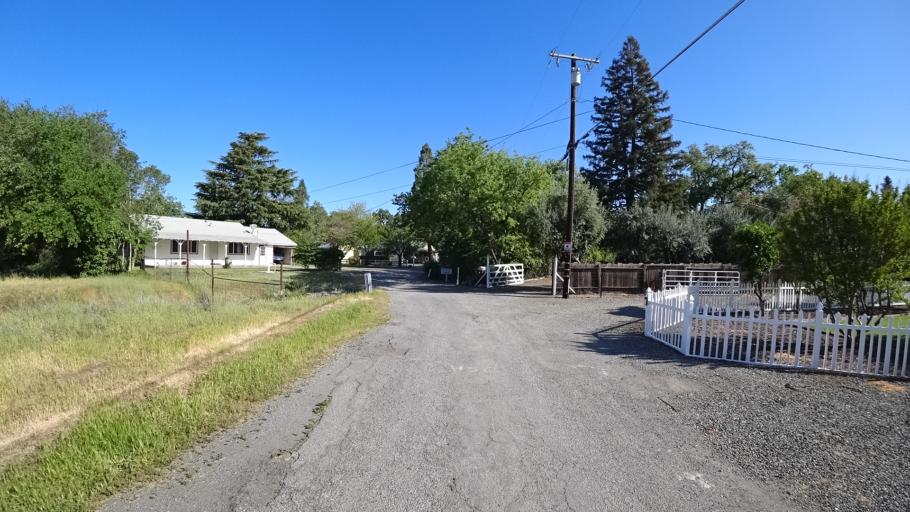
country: US
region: California
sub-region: Glenn County
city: Orland
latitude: 39.7563
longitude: -122.1889
